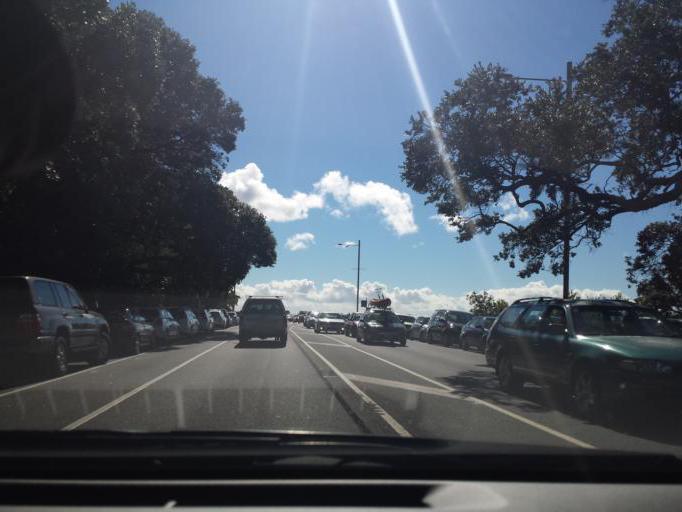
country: NZ
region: Auckland
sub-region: Auckland
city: Tamaki
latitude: -36.8469
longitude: 174.8286
